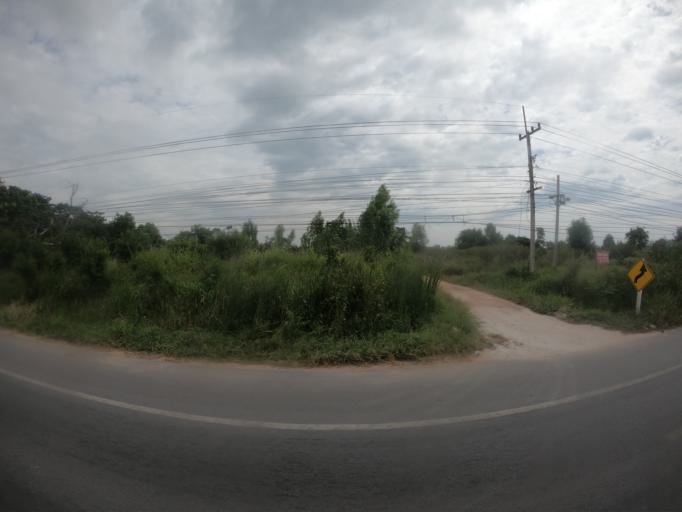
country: TH
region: Maha Sarakham
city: Kantharawichai
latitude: 16.2715
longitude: 103.2874
